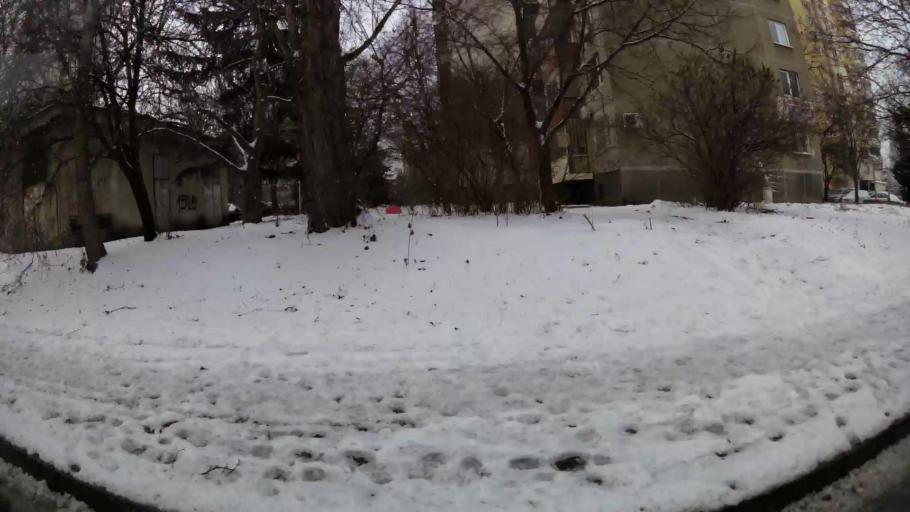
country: BG
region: Sofia-Capital
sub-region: Stolichna Obshtina
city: Sofia
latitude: 42.7162
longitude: 23.3055
